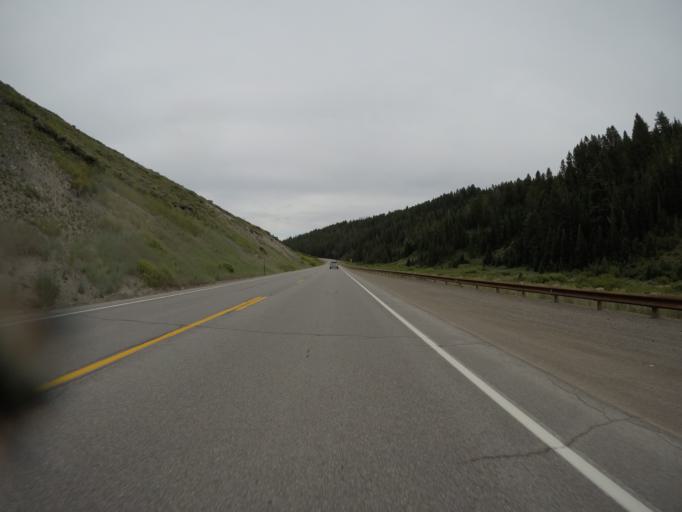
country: US
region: Wyoming
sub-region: Lincoln County
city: Afton
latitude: 42.4857
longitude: -110.9340
